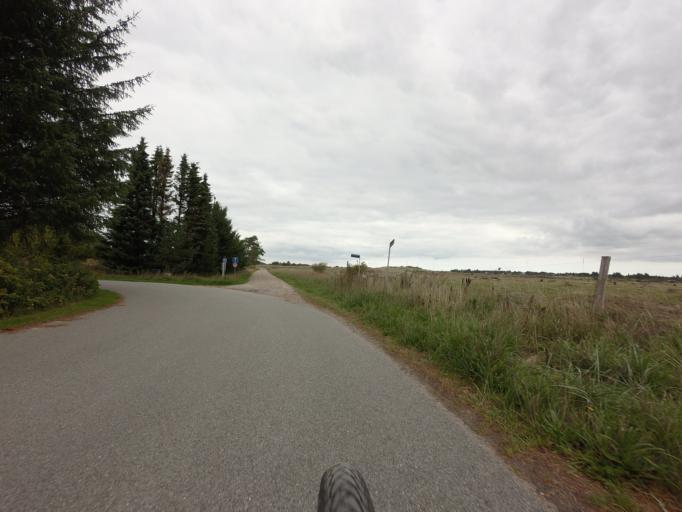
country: DK
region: North Denmark
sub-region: Hjorring Kommune
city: Sindal
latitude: 57.5856
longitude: 10.1712
